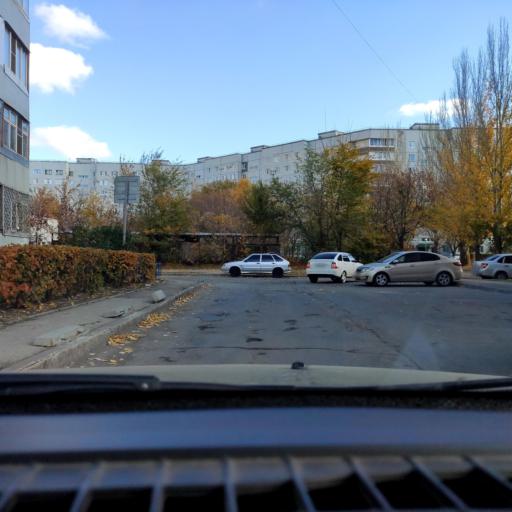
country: RU
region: Samara
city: Tol'yatti
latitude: 53.5037
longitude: 49.2798
